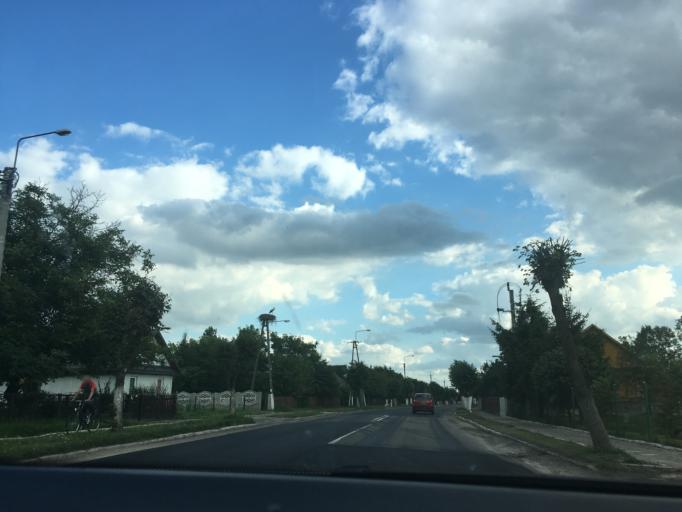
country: PL
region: Podlasie
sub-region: Powiat bielski
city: Bielsk Podlaski
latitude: 52.8094
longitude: 23.1945
